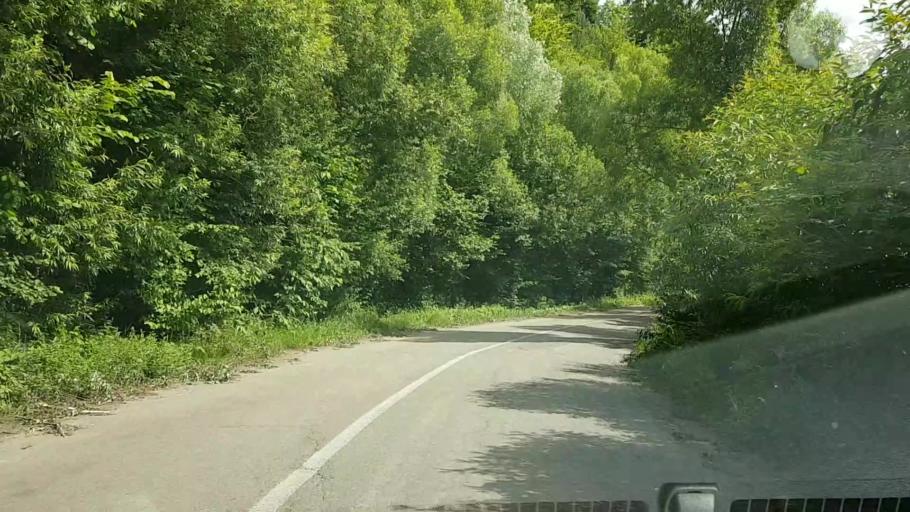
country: RO
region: Neamt
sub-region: Comuna Hangu
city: Hangu
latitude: 47.0283
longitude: 26.0681
